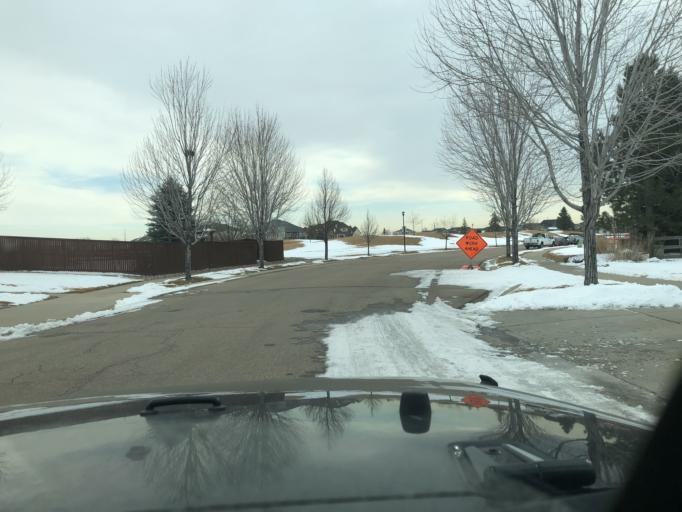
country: US
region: Colorado
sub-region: Boulder County
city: Longmont
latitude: 40.1908
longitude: -105.0644
